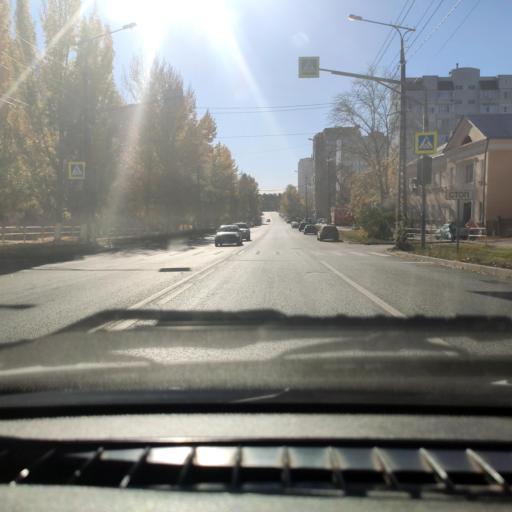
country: RU
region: Samara
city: Zhigulevsk
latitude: 53.4809
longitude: 49.4595
